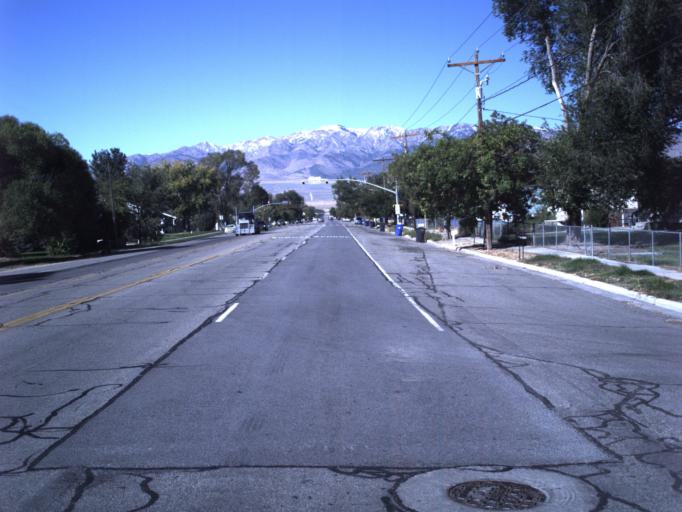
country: US
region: Utah
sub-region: Tooele County
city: Grantsville
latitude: 40.5998
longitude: -112.4469
